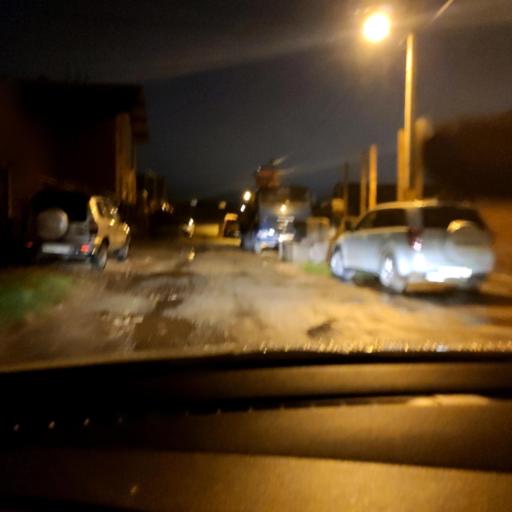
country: RU
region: Tatarstan
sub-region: Gorod Kazan'
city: Kazan
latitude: 55.8377
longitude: 49.2079
